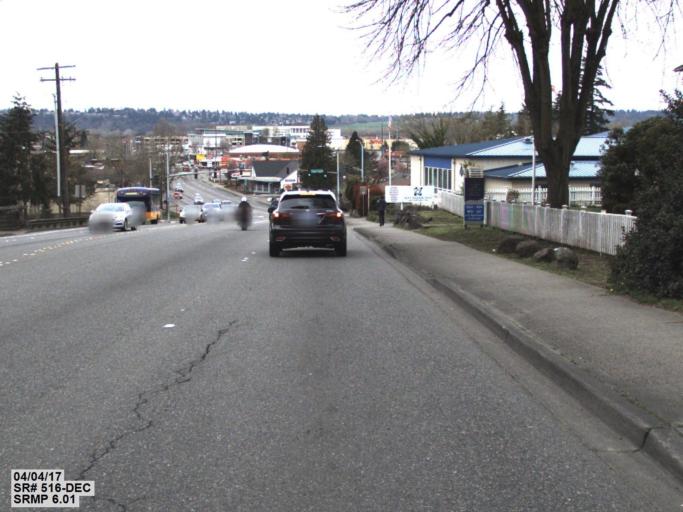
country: US
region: Washington
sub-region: King County
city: Kent
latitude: 47.3832
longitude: -122.2239
